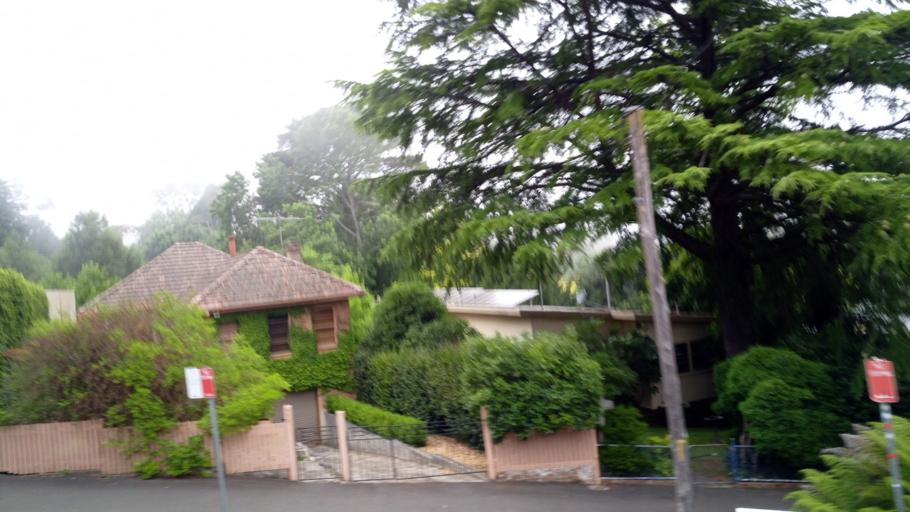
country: AU
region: New South Wales
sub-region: Blue Mountains Municipality
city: Leura
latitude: -33.7150
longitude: 150.3302
